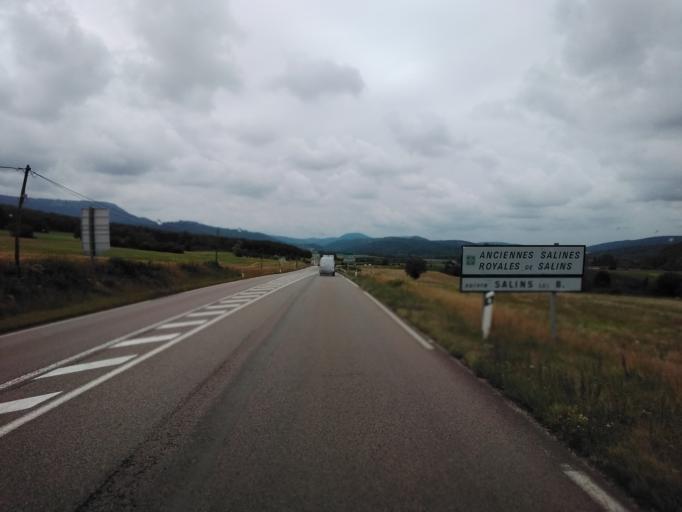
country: FR
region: Franche-Comte
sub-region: Departement du Doubs
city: Quingey
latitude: 47.0250
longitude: 5.8691
